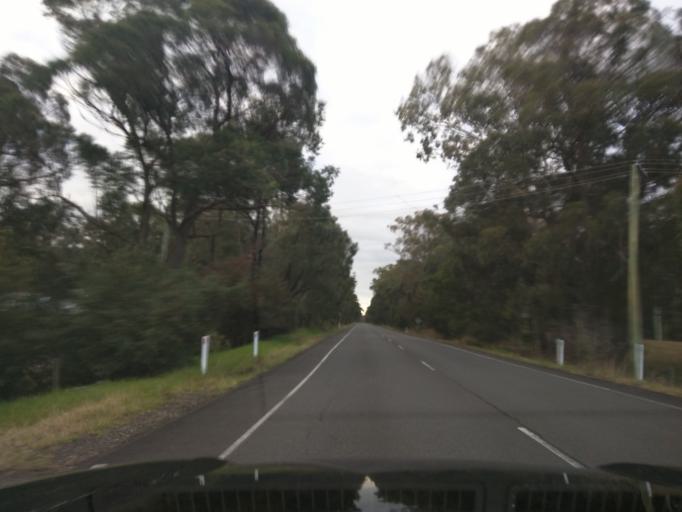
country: AU
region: New South Wales
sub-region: Wollondilly
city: Douglas Park
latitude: -34.2527
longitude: 150.7243
